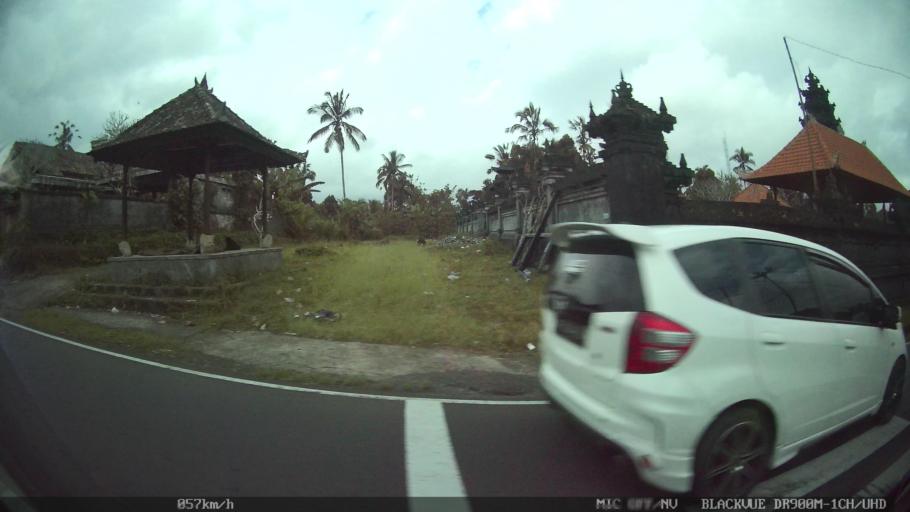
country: ID
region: Bali
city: Banjar Kubu
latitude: -8.3968
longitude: 115.4200
